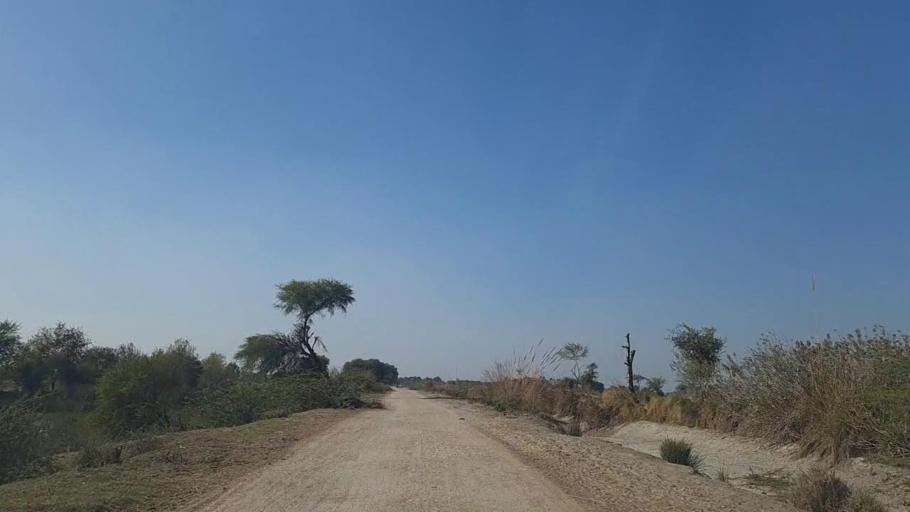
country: PK
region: Sindh
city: Shahpur Chakar
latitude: 26.2116
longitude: 68.6151
